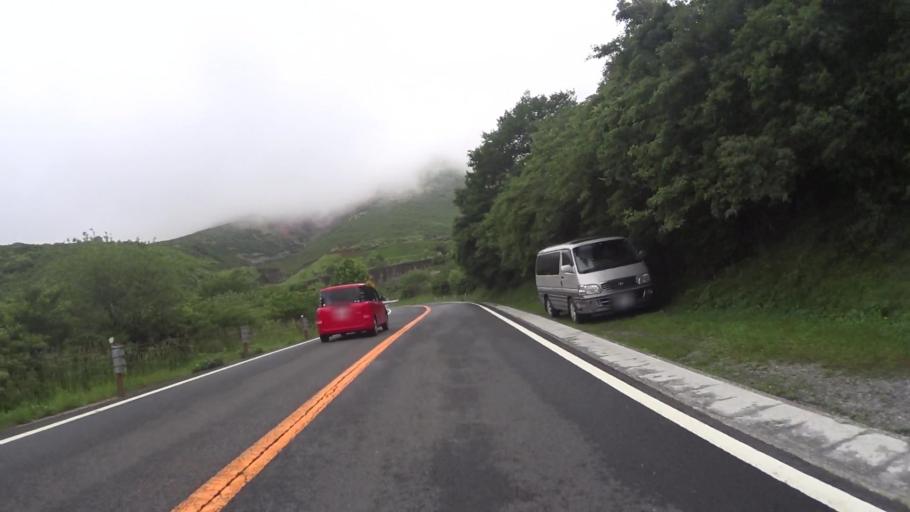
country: JP
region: Oita
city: Tsukawaki
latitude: 33.1019
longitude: 131.2254
